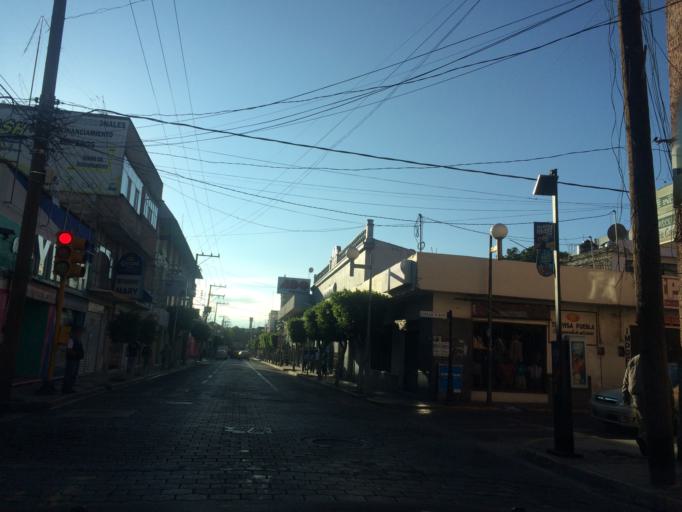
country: MX
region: Puebla
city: Tehuacan
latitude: 18.4631
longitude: -97.3967
